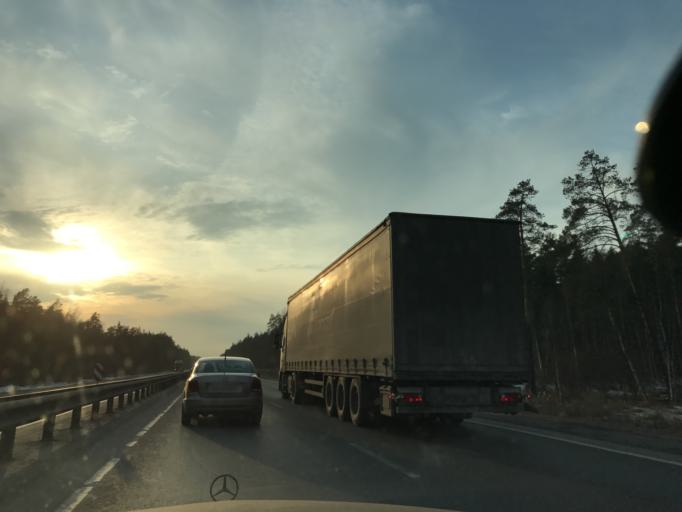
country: RU
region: Vladimir
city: Petushki
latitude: 55.9296
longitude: 39.3430
